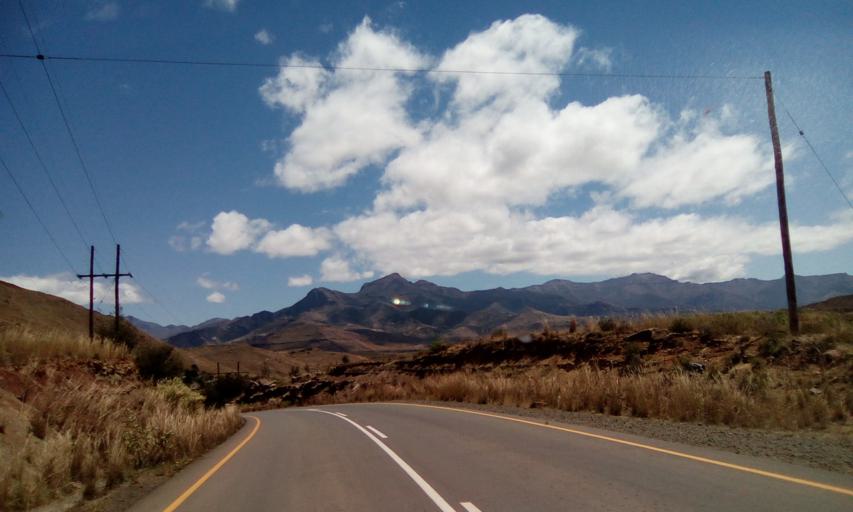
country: LS
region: Qacha's Nek
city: Qacha's Nek
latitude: -30.0799
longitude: 28.6257
